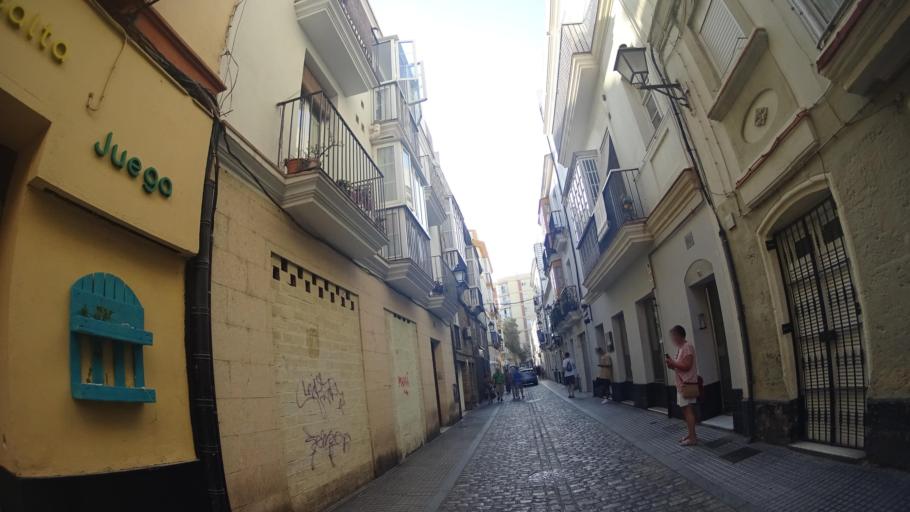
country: ES
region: Andalusia
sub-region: Provincia de Cadiz
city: Cadiz
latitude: 36.5311
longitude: -6.3019
